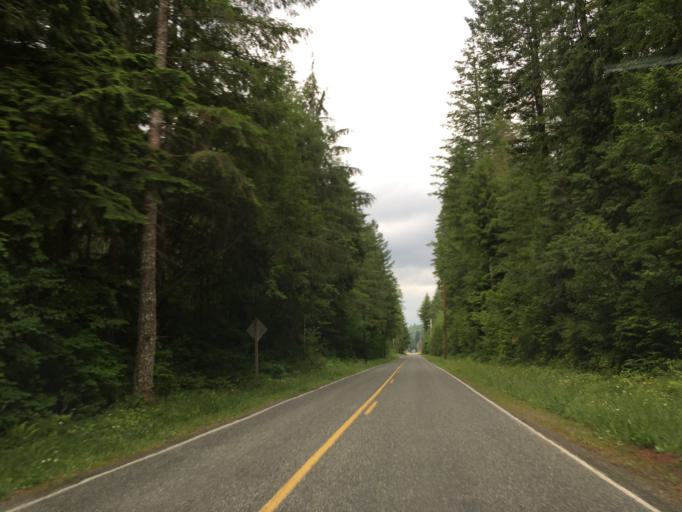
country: US
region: Washington
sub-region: Whatcom County
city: Peaceful Valley
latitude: 48.9733
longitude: -122.1428
